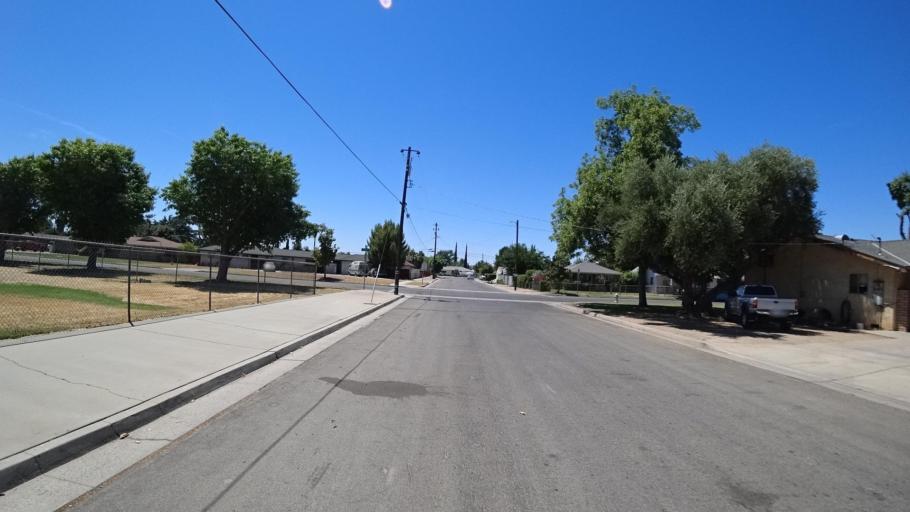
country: US
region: California
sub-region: Fresno County
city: Sunnyside
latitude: 36.7489
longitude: -119.7341
